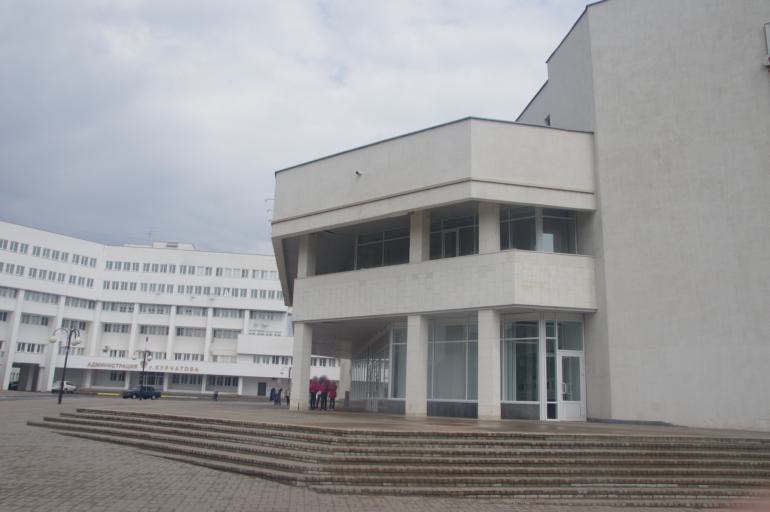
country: RU
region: Kursk
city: Kurchatov
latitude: 51.6589
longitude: 35.6594
